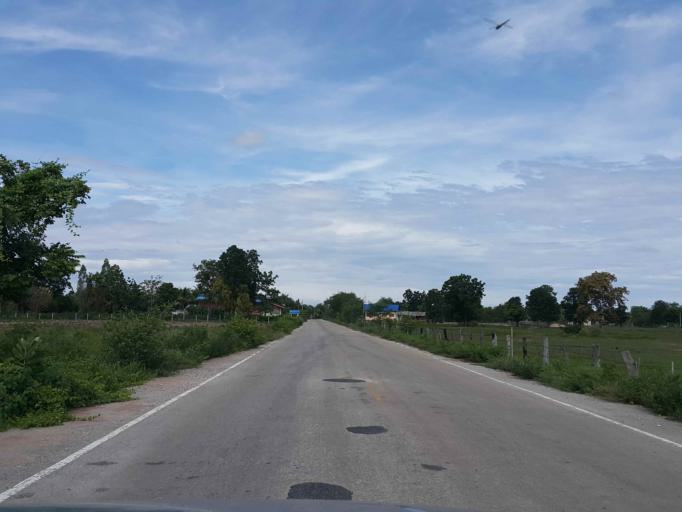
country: TH
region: Sukhothai
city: Ban Dan Lan Hoi
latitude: 17.1090
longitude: 99.4842
